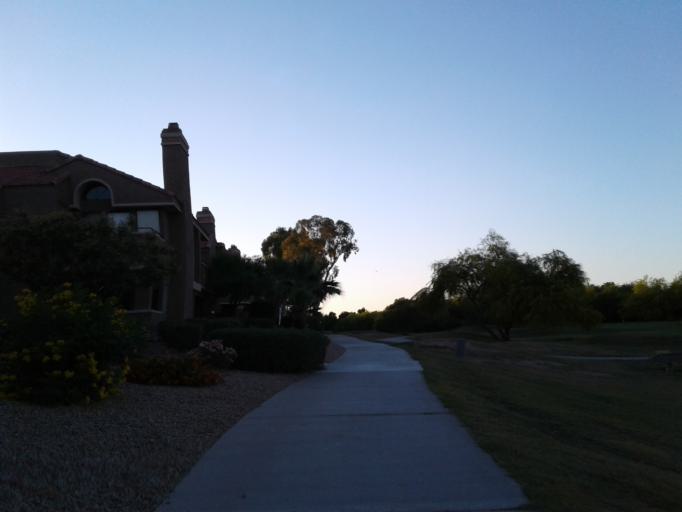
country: US
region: Arizona
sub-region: Maricopa County
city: Paradise Valley
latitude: 33.5849
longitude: -111.9719
